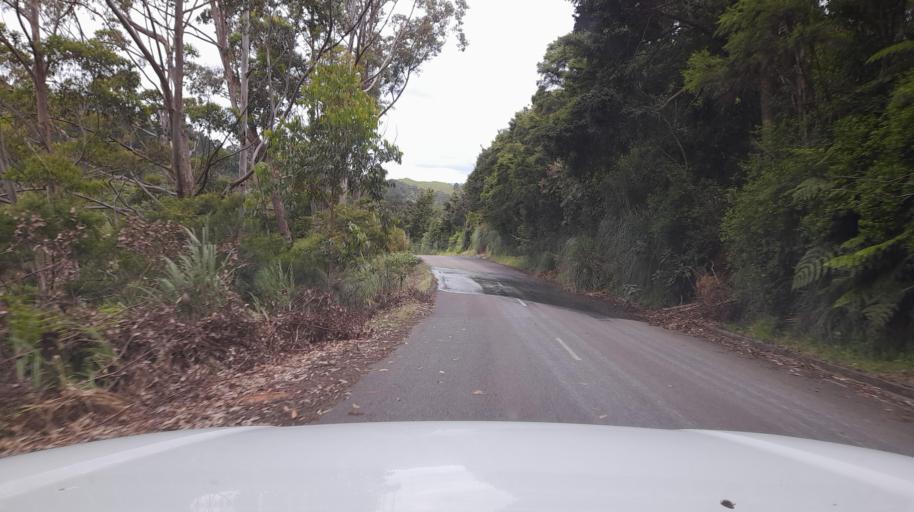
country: NZ
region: Northland
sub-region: Far North District
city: Kaitaia
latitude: -35.3563
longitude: 173.4654
